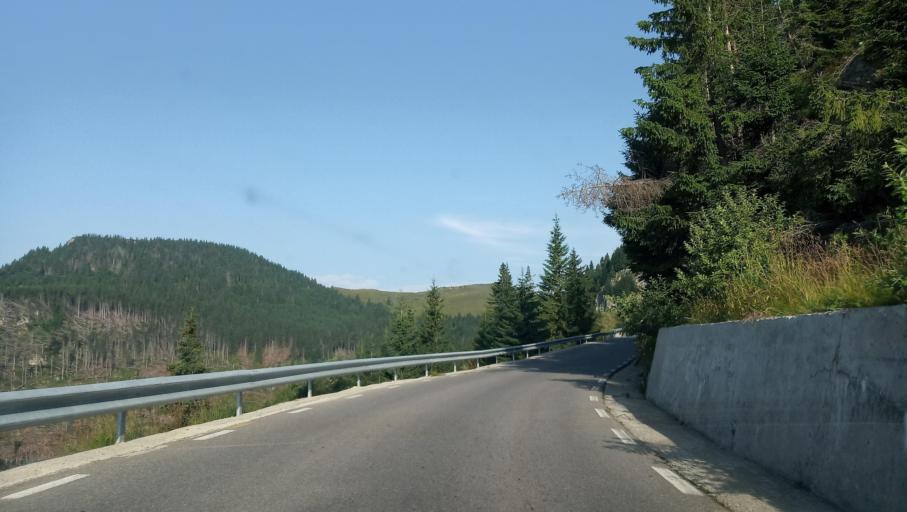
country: RO
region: Prahova
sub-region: Oras Sinaia
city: Sinaia
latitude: 45.3201
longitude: 25.4788
